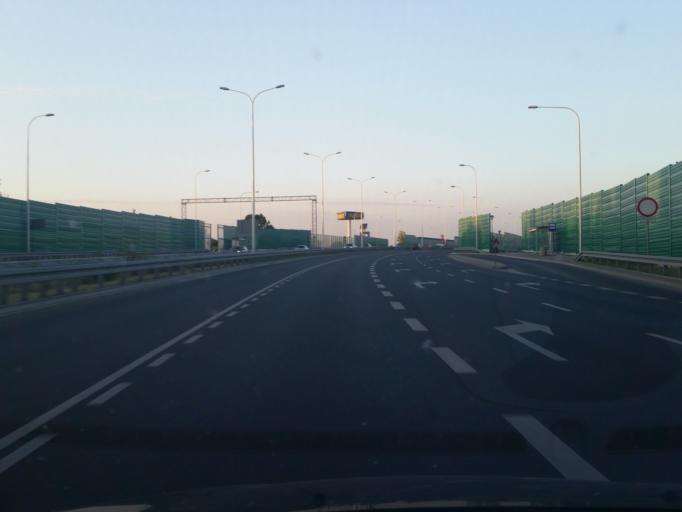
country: PL
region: Masovian Voivodeship
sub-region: Warszawa
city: Bielany
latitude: 52.2972
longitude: 20.9341
